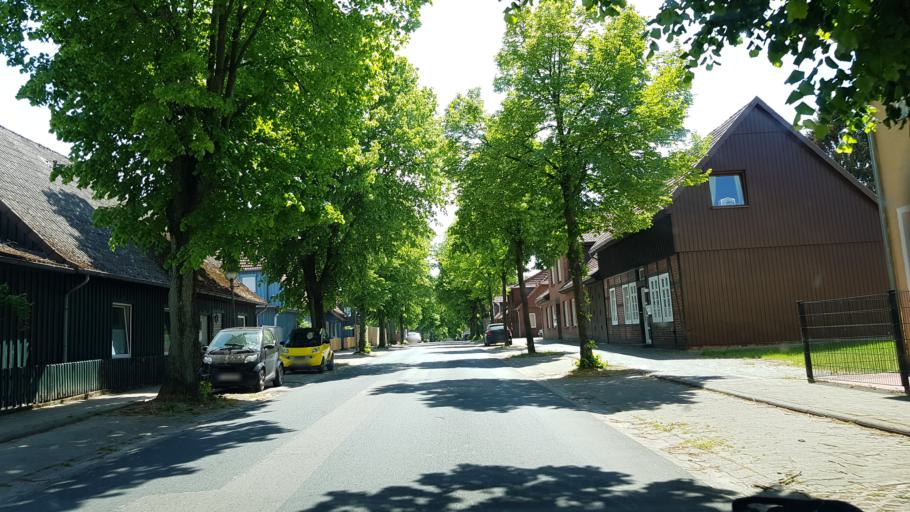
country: DE
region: Lower Saxony
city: Eschede
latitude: 52.7383
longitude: 10.2320
